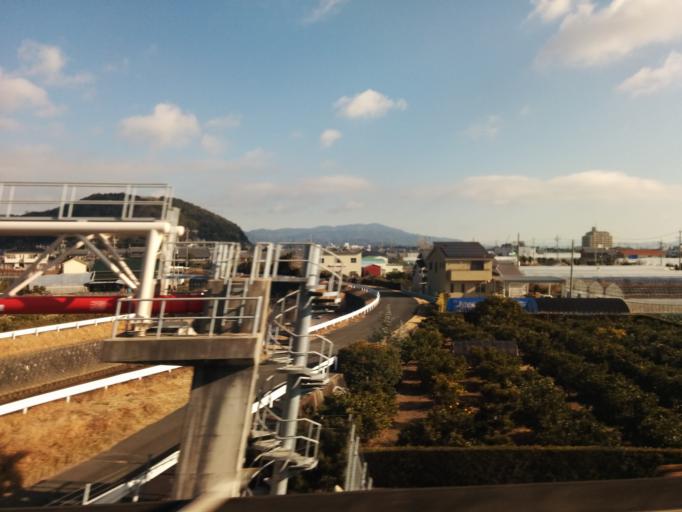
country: JP
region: Aichi
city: Kozakai-cho
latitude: 34.8093
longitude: 137.3069
